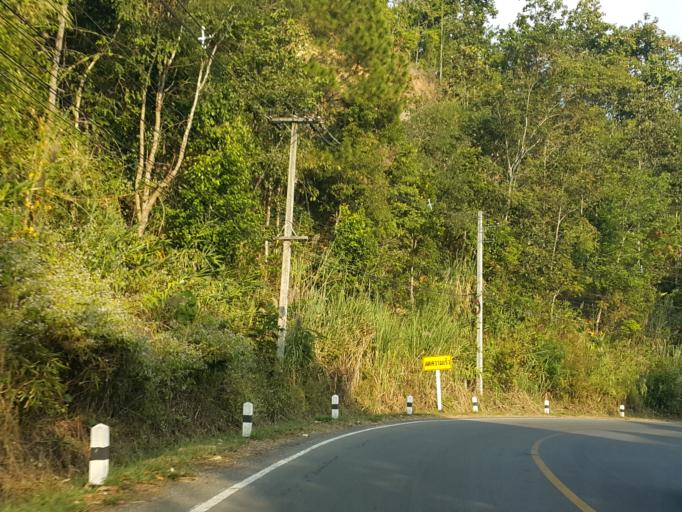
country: TH
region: Chiang Mai
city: Samoeng
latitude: 18.8990
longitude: 98.8574
